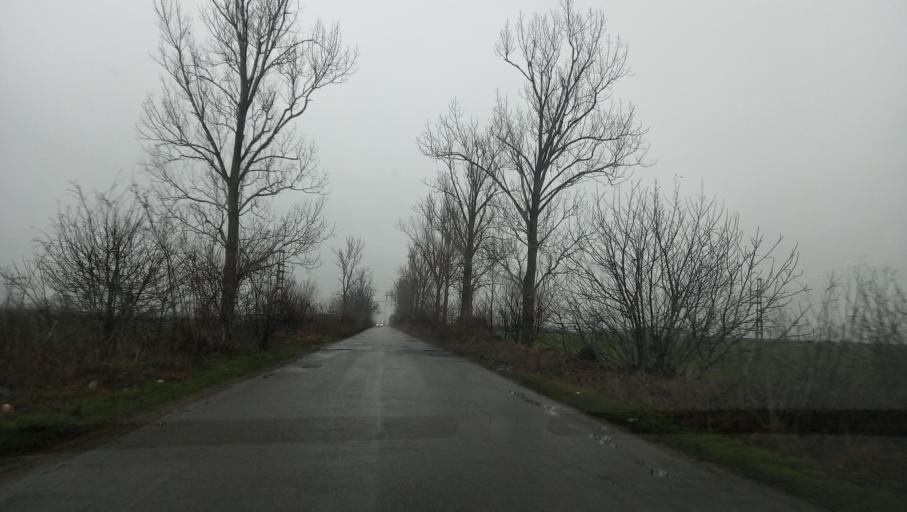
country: RO
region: Giurgiu
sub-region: Comuna Herasti
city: Herasti
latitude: 44.2476
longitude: 26.3656
